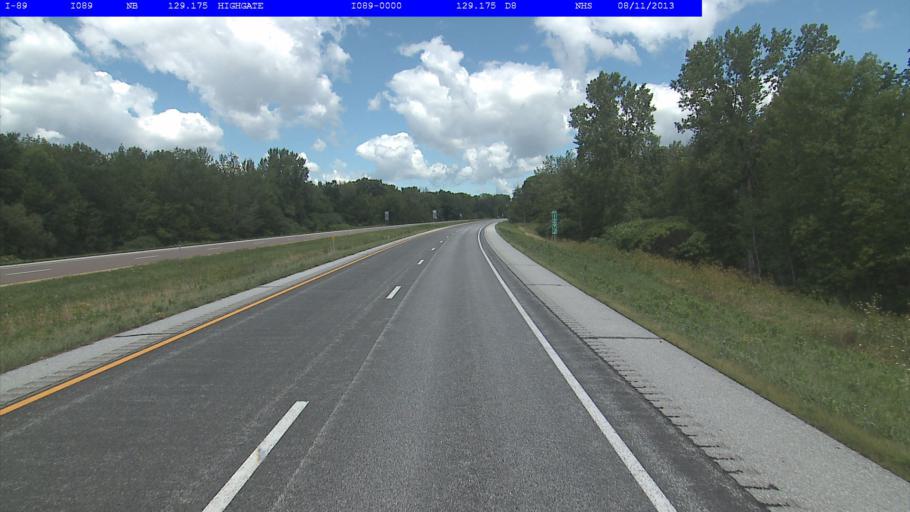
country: US
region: Vermont
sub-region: Franklin County
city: Swanton
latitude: 45.0000
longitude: -73.0866
